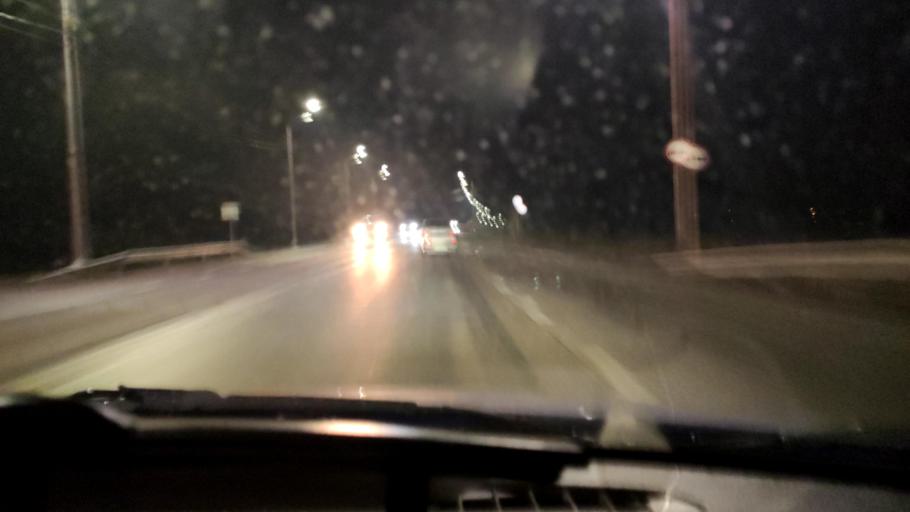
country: RU
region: Voronezj
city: Devitsa
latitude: 51.6321
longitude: 38.9854
